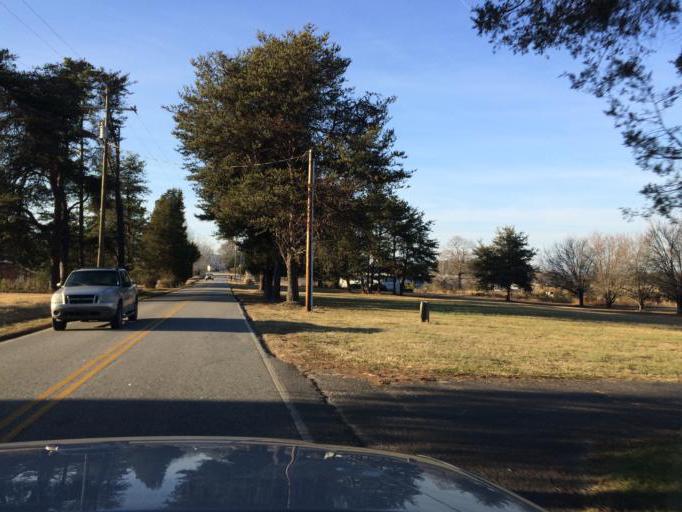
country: US
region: South Carolina
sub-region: Spartanburg County
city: Landrum
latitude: 35.1430
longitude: -82.1018
